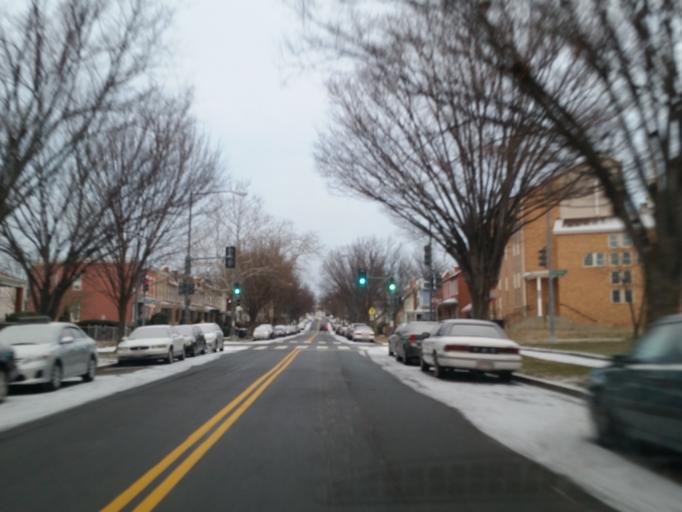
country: US
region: Maryland
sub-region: Montgomery County
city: Takoma Park
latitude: 38.9537
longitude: -77.0259
